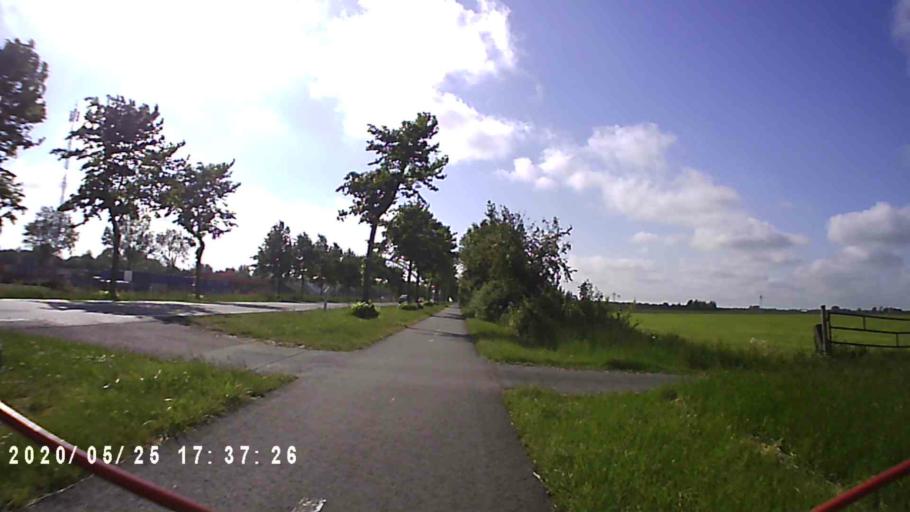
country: NL
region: Groningen
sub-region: Gemeente Groningen
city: Korrewegwijk
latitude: 53.2415
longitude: 6.5621
